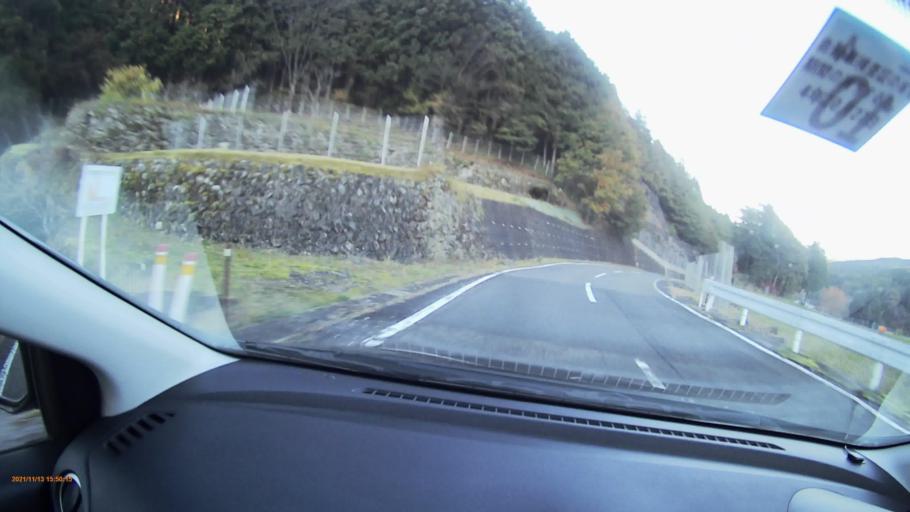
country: JP
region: Gifu
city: Nakatsugawa
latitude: 35.5974
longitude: 137.4096
